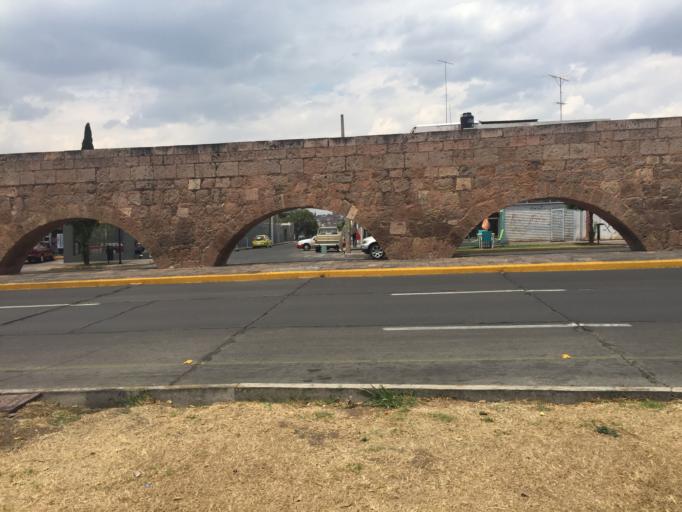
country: MX
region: Michoacan
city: Morelia
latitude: 19.6977
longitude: -101.1740
